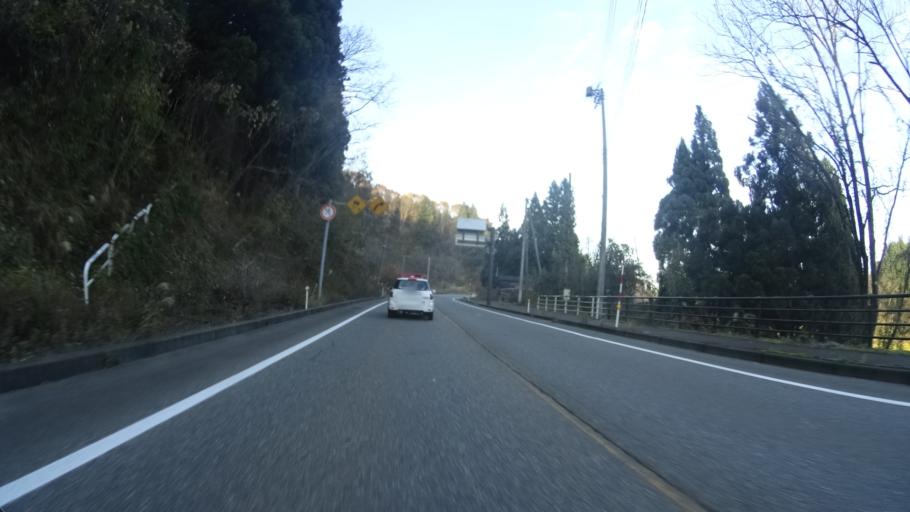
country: JP
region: Niigata
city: Nagaoka
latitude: 37.4146
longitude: 138.7136
